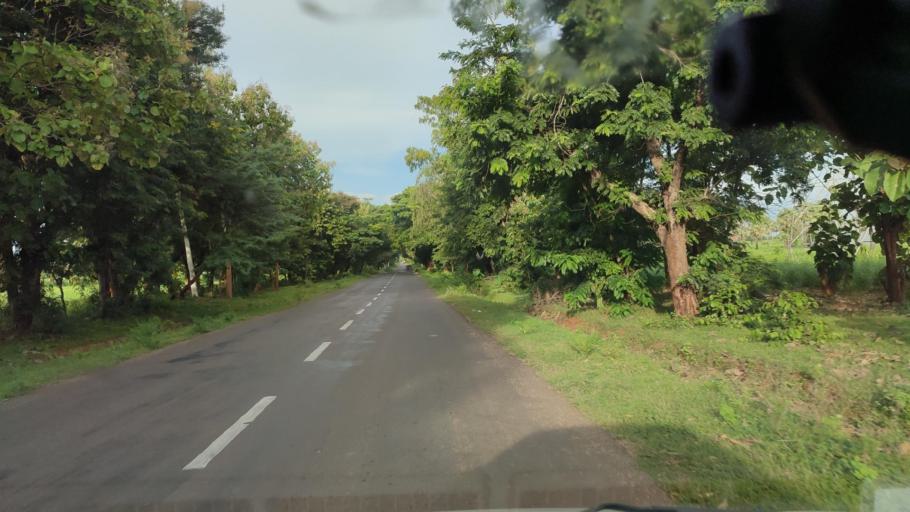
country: MM
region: Magway
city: Chauk
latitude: 20.8102
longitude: 95.0412
